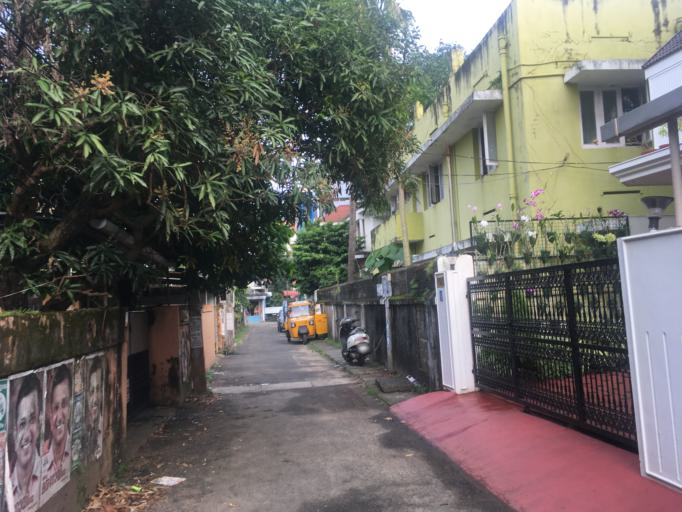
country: IN
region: Kerala
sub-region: Ernakulam
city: Cochin
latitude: 9.9903
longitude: 76.2782
